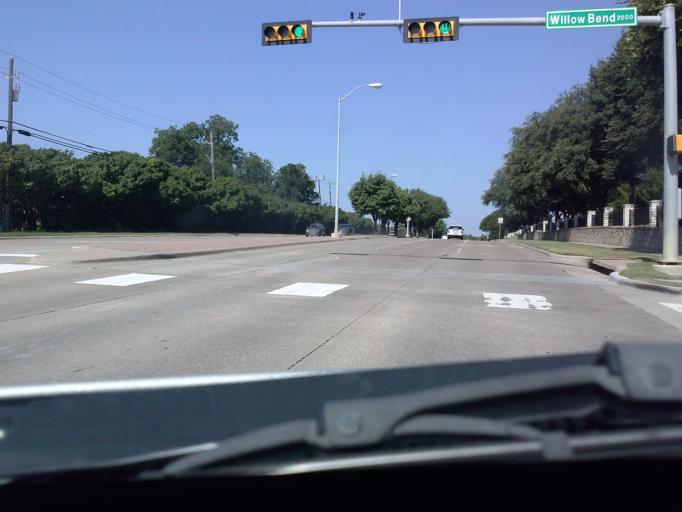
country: US
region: Texas
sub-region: Dallas County
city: Addison
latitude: 33.0280
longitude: -96.8142
